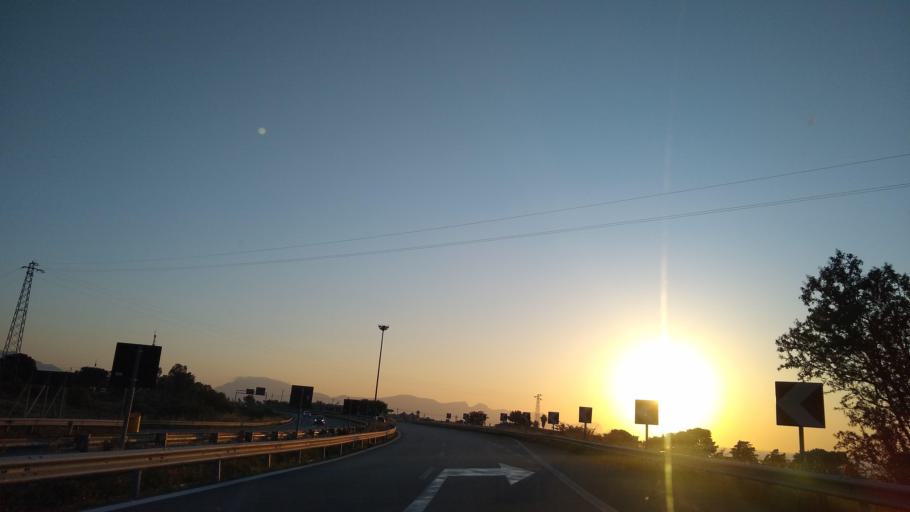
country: IT
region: Sicily
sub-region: Palermo
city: Terrasini
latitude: 38.1368
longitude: 13.0807
